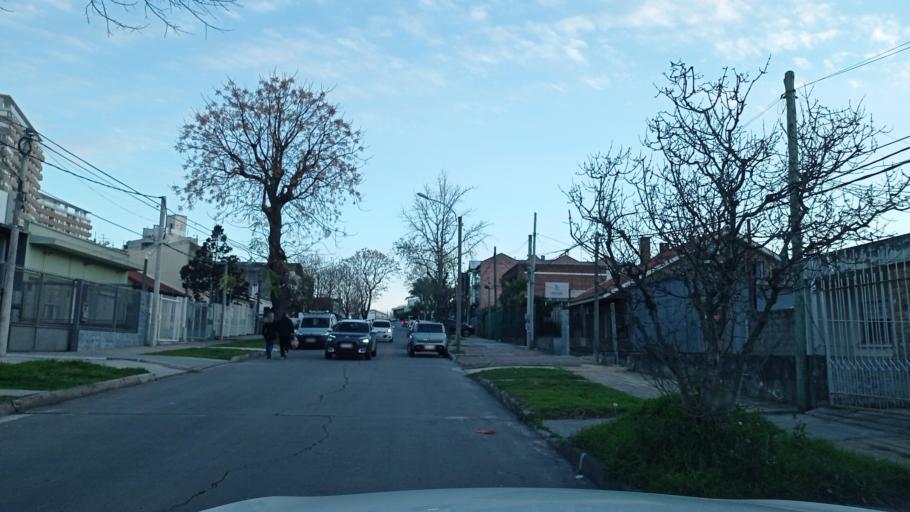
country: UY
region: Montevideo
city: Montevideo
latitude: -34.8859
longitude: -56.1195
